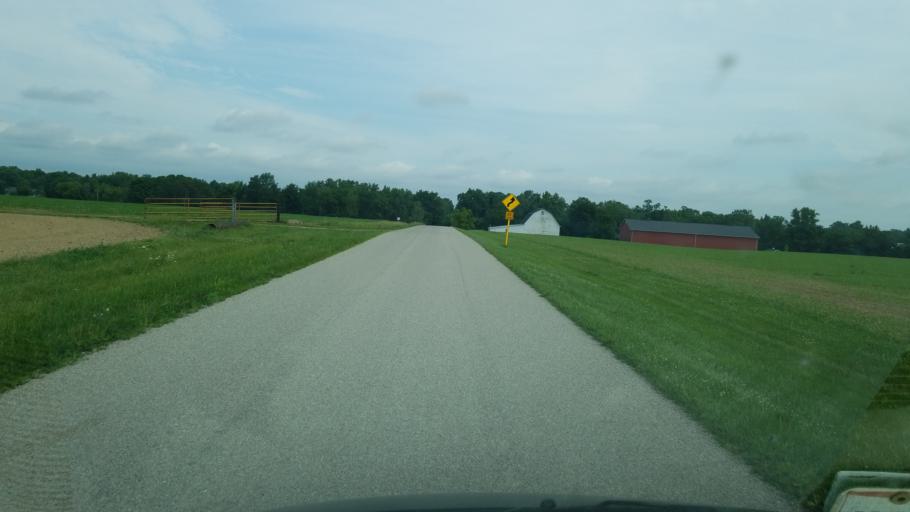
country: US
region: Ohio
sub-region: Seneca County
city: Tiffin
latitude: 41.1487
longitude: -83.0944
